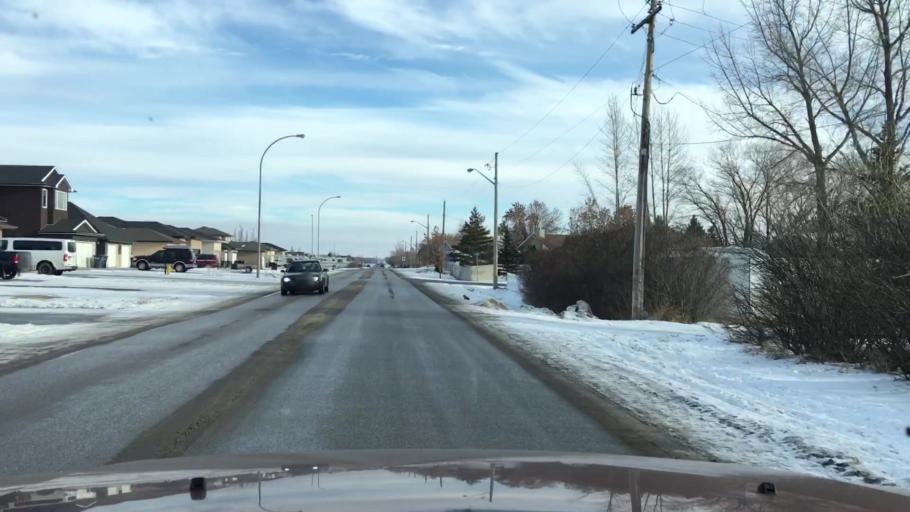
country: CA
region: Saskatchewan
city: Pilot Butte
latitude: 50.4843
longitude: -104.4197
